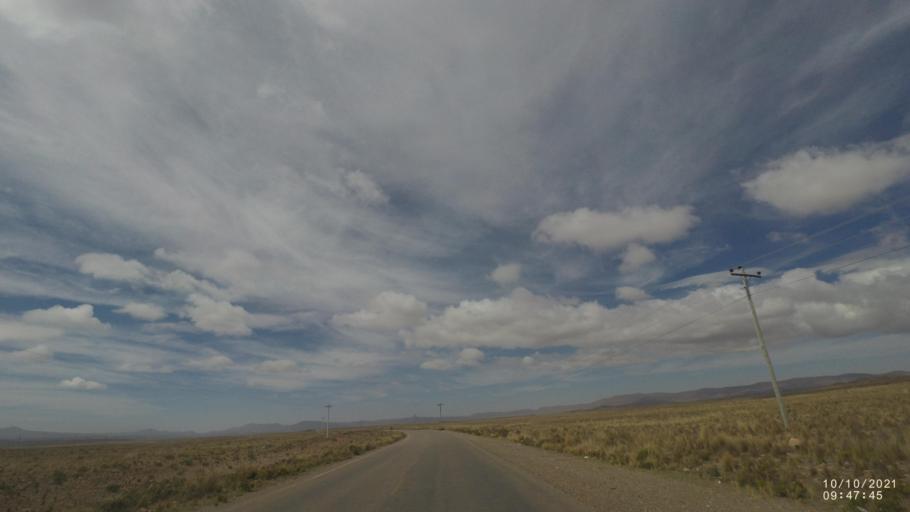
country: BO
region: La Paz
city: Quime
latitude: -17.1986
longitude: -67.3421
